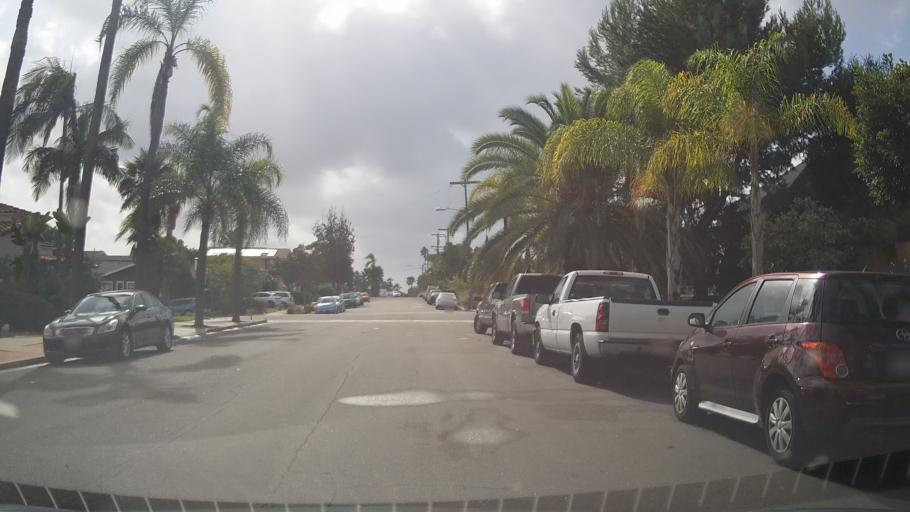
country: US
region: California
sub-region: San Diego County
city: San Diego
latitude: 32.7312
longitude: -117.1244
